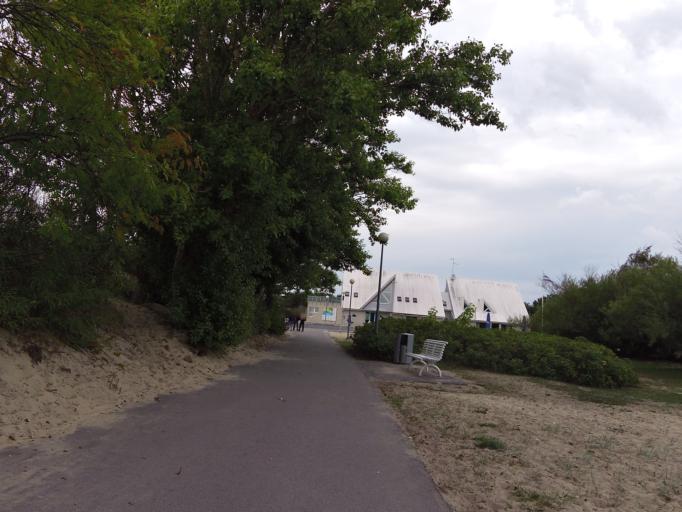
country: EE
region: Harju
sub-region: Tallinna linn
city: Tallinn
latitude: 59.4416
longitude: 24.6840
